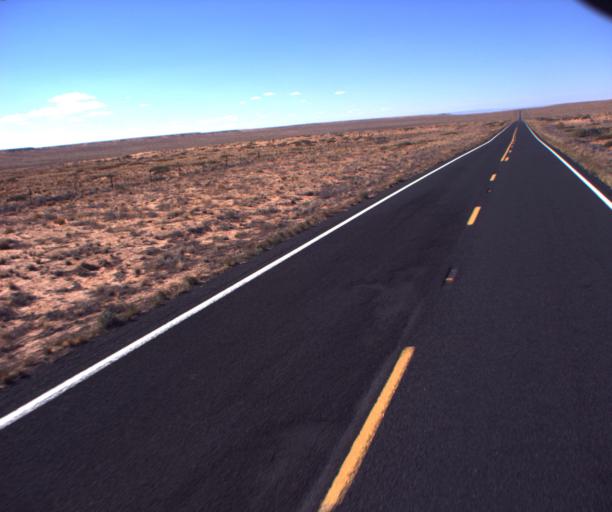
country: US
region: Arizona
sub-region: Coconino County
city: Tuba City
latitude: 36.0242
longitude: -111.1422
